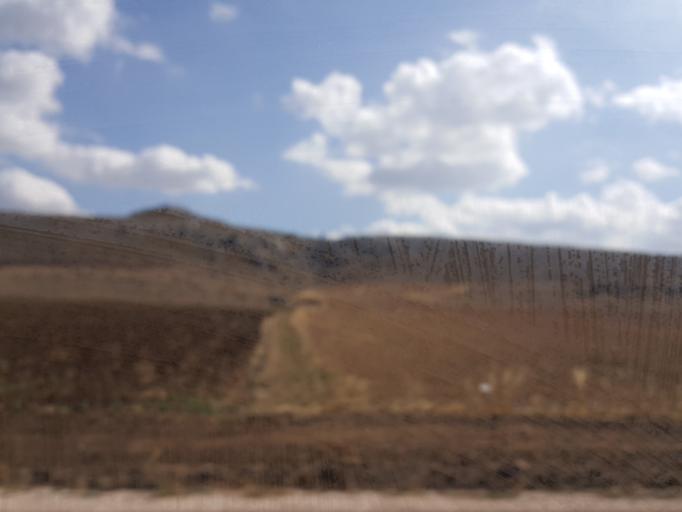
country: TR
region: Tokat
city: Artova
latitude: 40.1405
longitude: 36.3635
